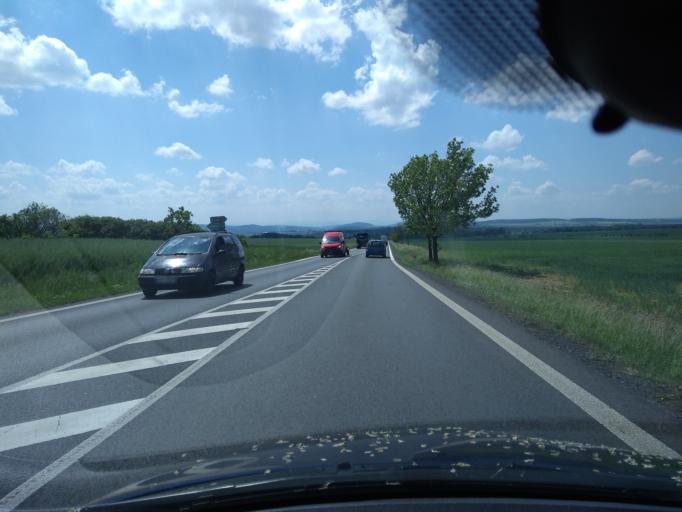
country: CZ
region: Plzensky
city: Chlumcany
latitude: 49.6289
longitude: 13.3310
